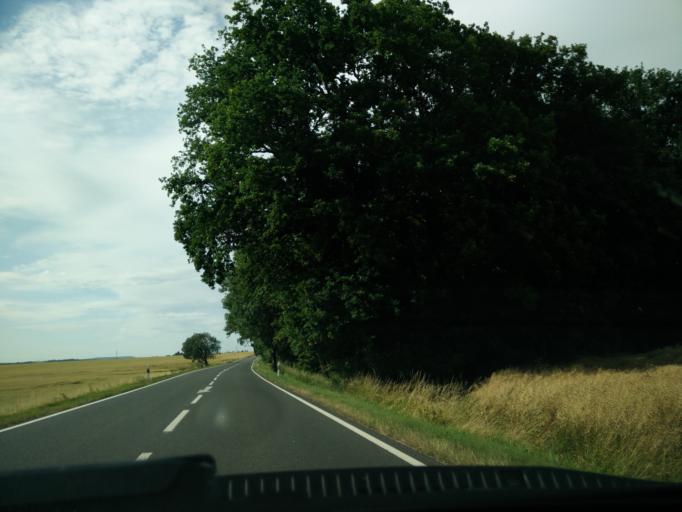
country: DE
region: Saxony
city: Geithain
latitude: 51.0685
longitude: 12.6673
